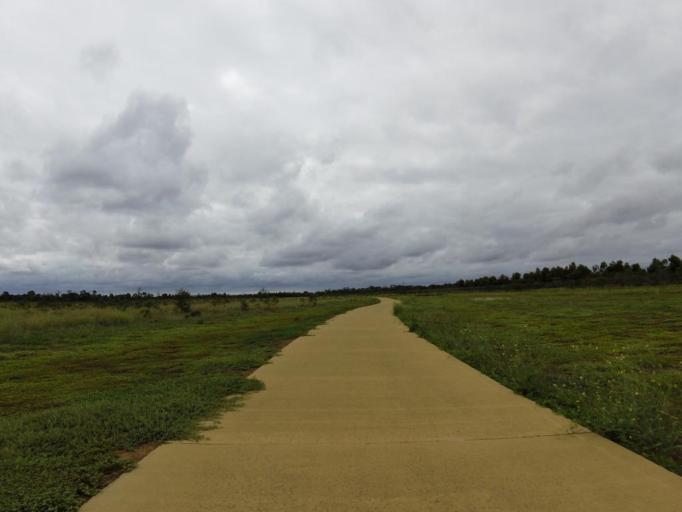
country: AU
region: Victoria
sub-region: Wyndham
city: Werribee
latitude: -37.9291
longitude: 144.6564
